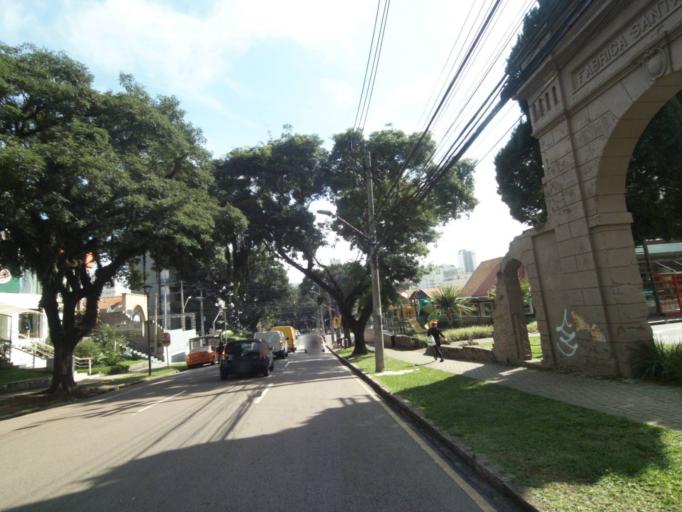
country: BR
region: Parana
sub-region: Curitiba
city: Curitiba
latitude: -25.4408
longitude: -49.2820
